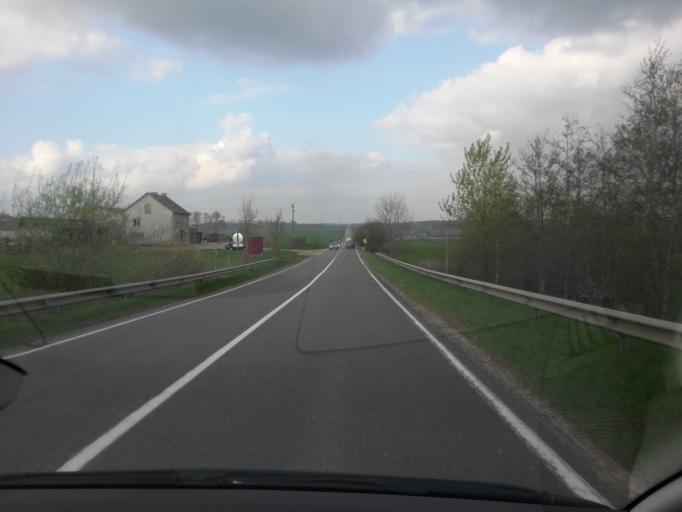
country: BE
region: Wallonia
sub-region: Province du Luxembourg
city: Etalle
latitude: 49.6827
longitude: 5.6055
